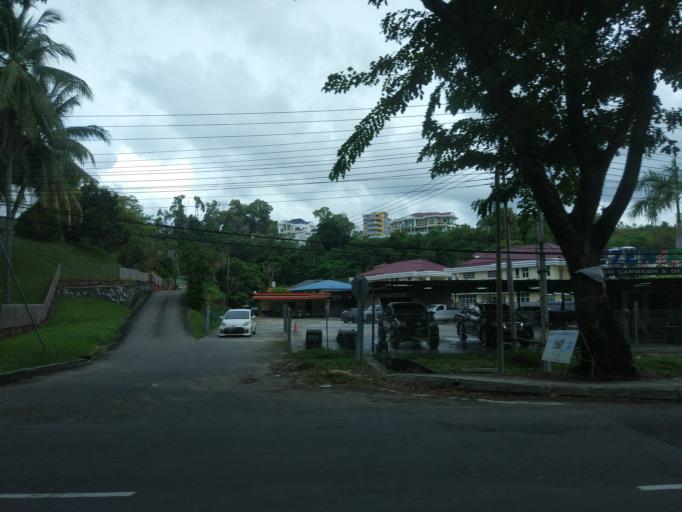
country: MY
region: Sabah
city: Kota Kinabalu
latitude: 5.9779
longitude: 116.0983
